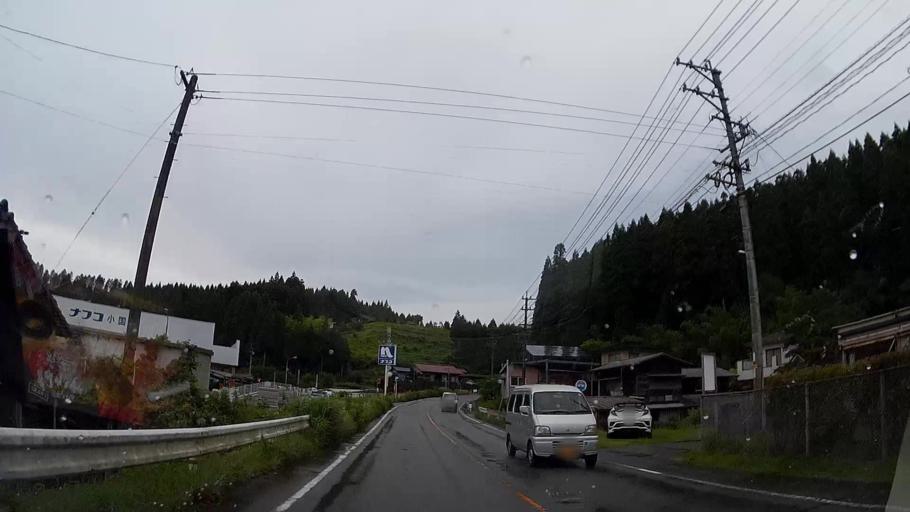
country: JP
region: Oita
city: Tsukawaki
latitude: 33.1351
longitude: 131.0629
